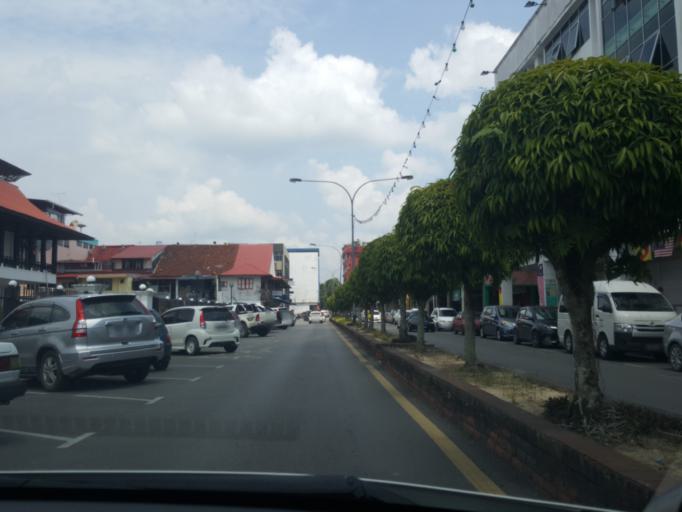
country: MY
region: Sarawak
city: Sarikei
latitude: 2.1326
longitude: 111.5225
